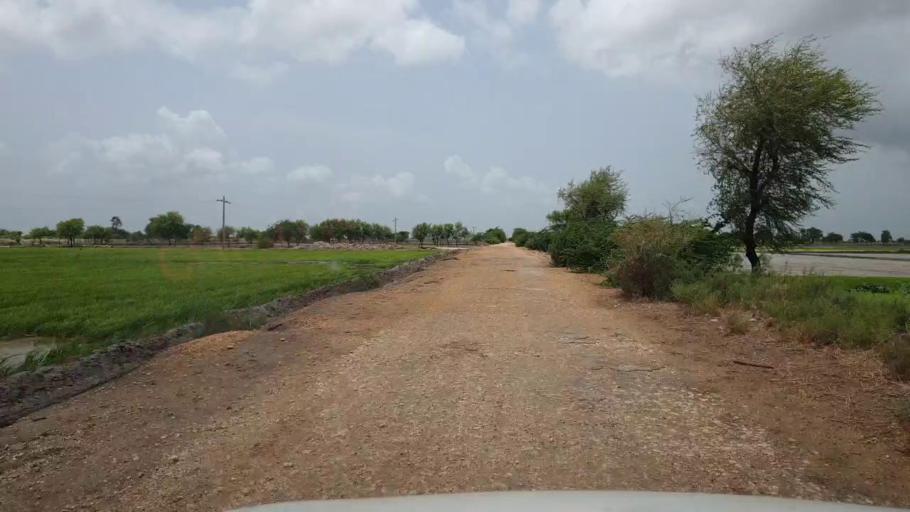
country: PK
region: Sindh
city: Kario
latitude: 24.7554
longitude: 68.4577
